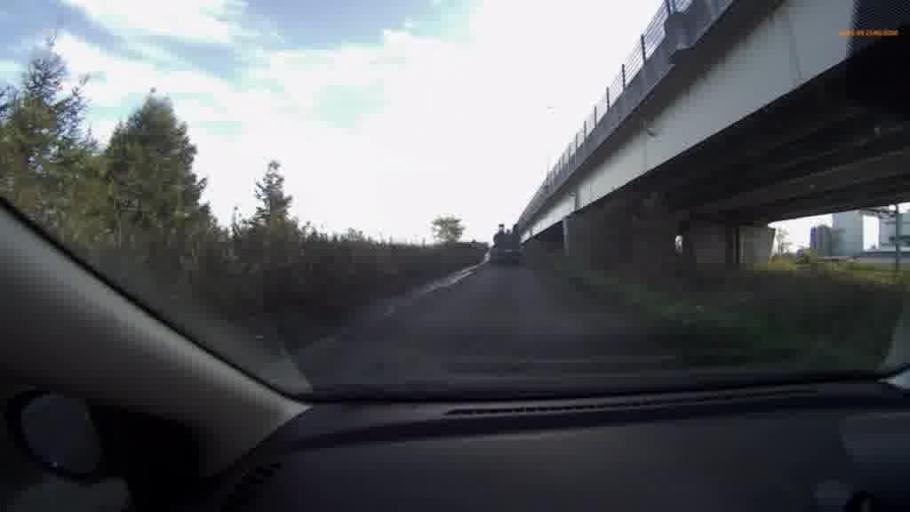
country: JP
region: Hokkaido
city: Kushiro
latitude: 43.0212
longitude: 144.2636
